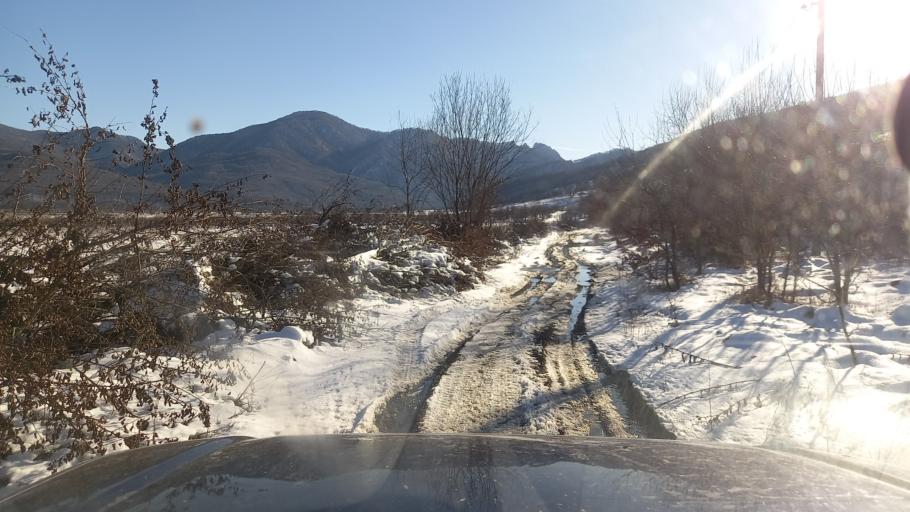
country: RU
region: Adygeya
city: Kamennomostskiy
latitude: 44.2025
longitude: 40.1511
